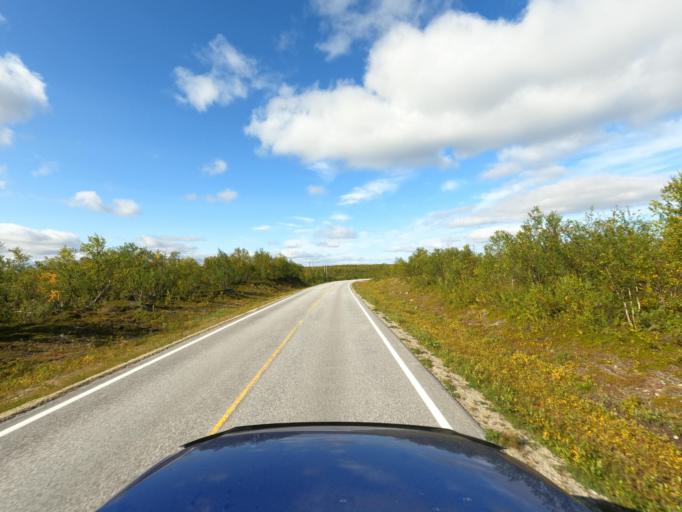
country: NO
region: Finnmark Fylke
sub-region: Karasjok
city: Karasjohka
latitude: 69.6100
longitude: 25.3117
